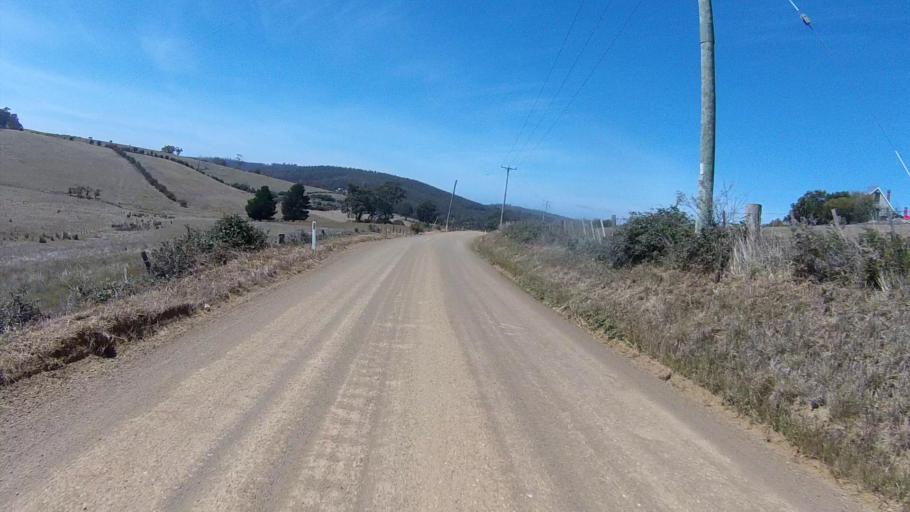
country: AU
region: Tasmania
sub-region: Sorell
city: Sorell
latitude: -42.7923
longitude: 147.6386
